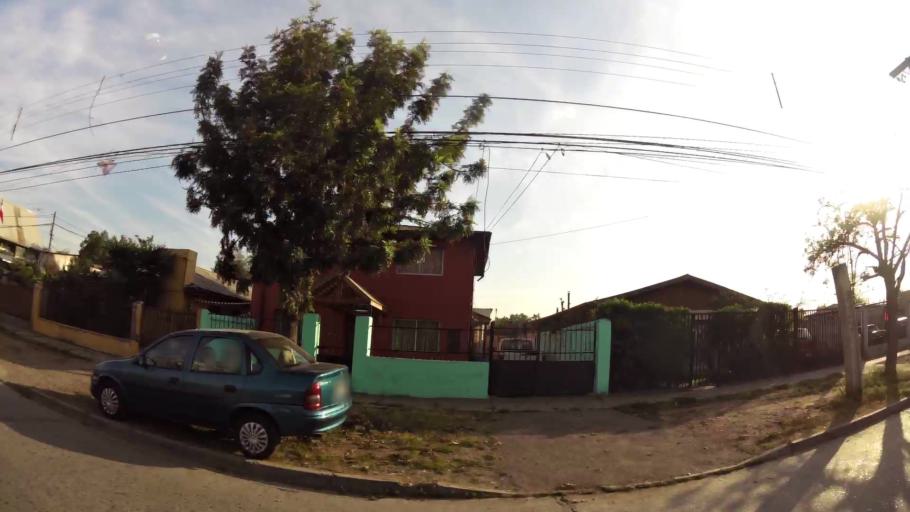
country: CL
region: Santiago Metropolitan
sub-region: Provincia de Maipo
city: San Bernardo
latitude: -33.5286
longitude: -70.6775
